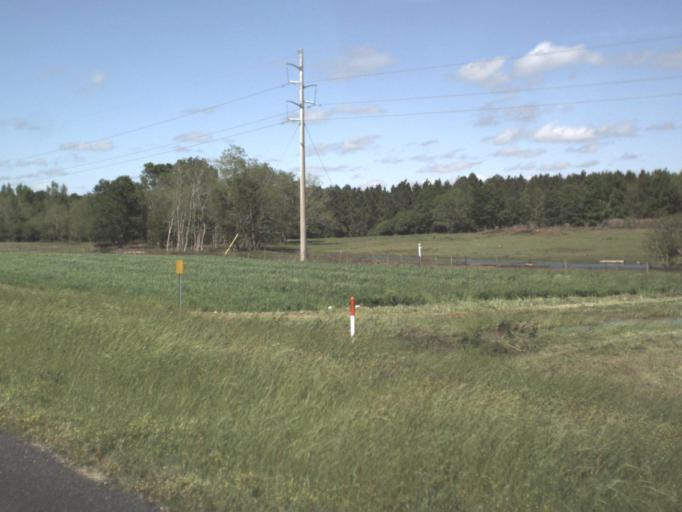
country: US
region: Florida
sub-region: Escambia County
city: Molino
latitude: 30.7260
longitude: -87.3493
